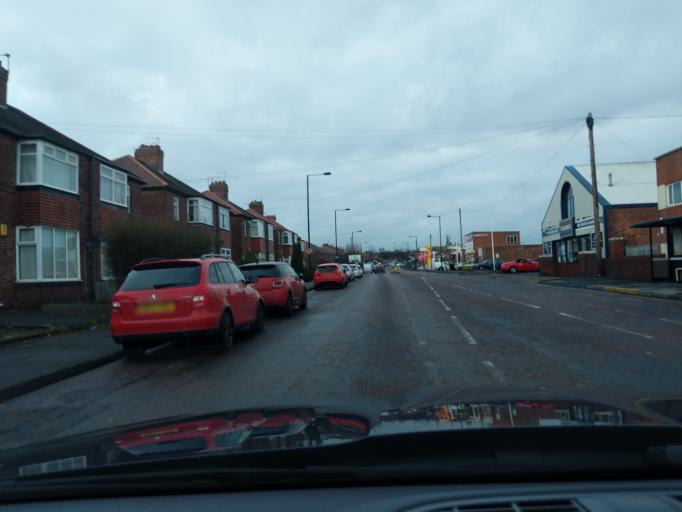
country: GB
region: England
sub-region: Borough of North Tyneside
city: Wallsend
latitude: 54.9923
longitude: -1.5640
